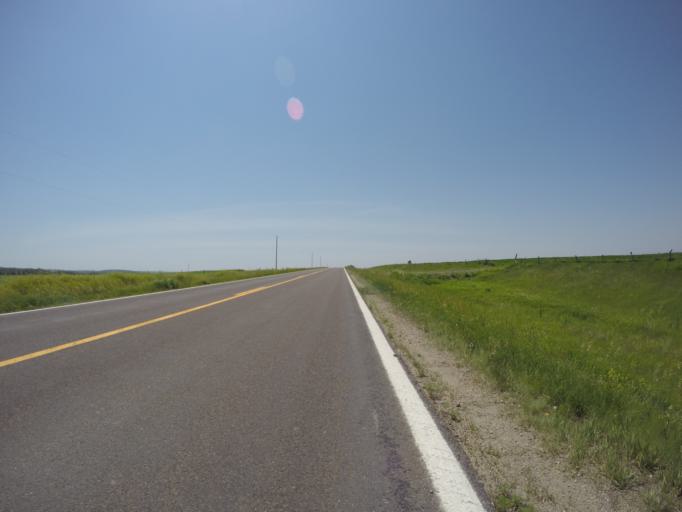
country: US
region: Nebraska
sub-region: Pawnee County
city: Pawnee City
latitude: 40.0210
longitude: -96.0483
